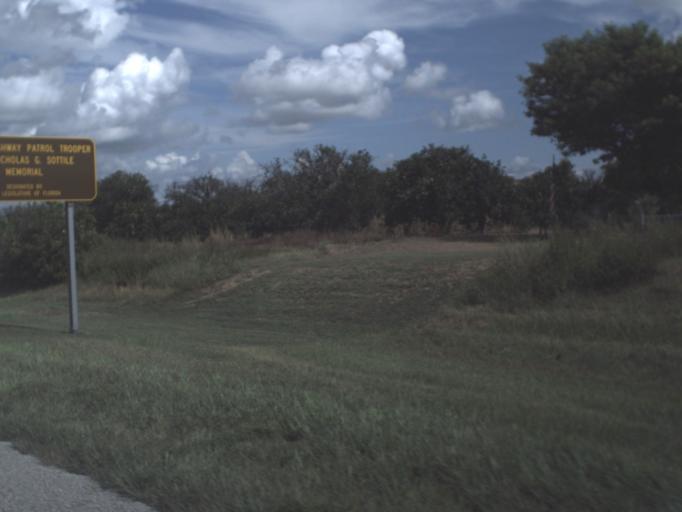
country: US
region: Florida
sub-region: Highlands County
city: Lake Placid
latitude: 27.3376
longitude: -81.3857
